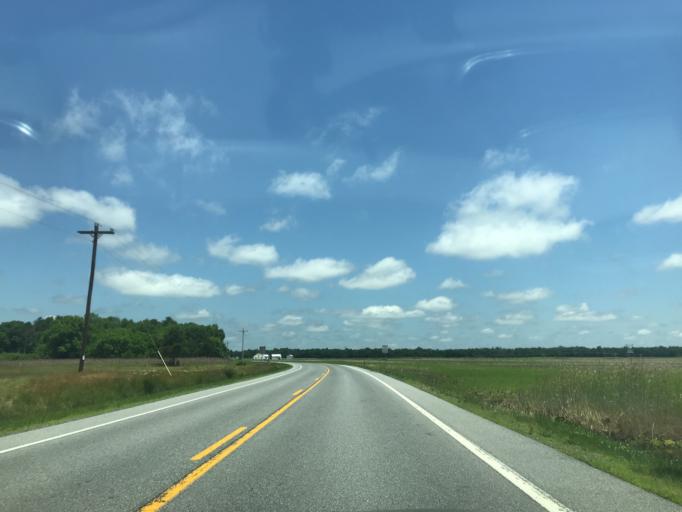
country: US
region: Maryland
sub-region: Caroline County
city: Federalsburg
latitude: 38.7205
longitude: -75.7367
